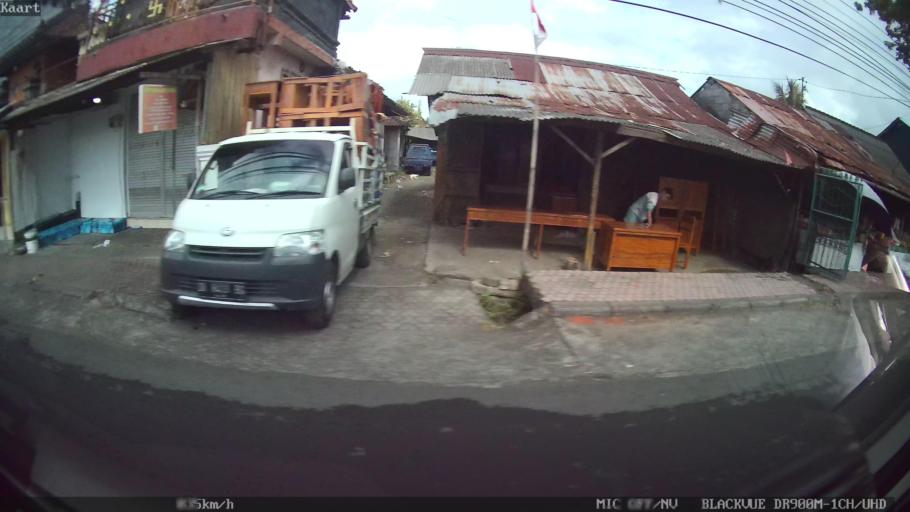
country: ID
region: Bali
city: Banjar Kertasari
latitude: -8.6216
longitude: 115.2099
